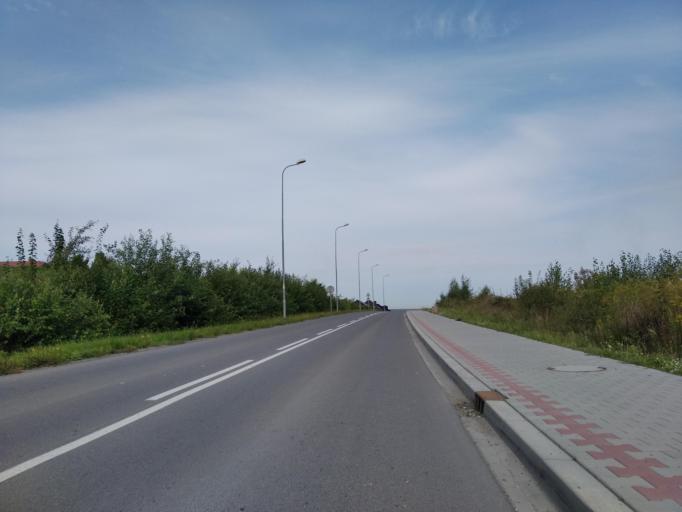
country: PL
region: Subcarpathian Voivodeship
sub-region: Powiat ropczycko-sedziszowski
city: Ropczyce
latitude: 50.0635
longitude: 21.6079
